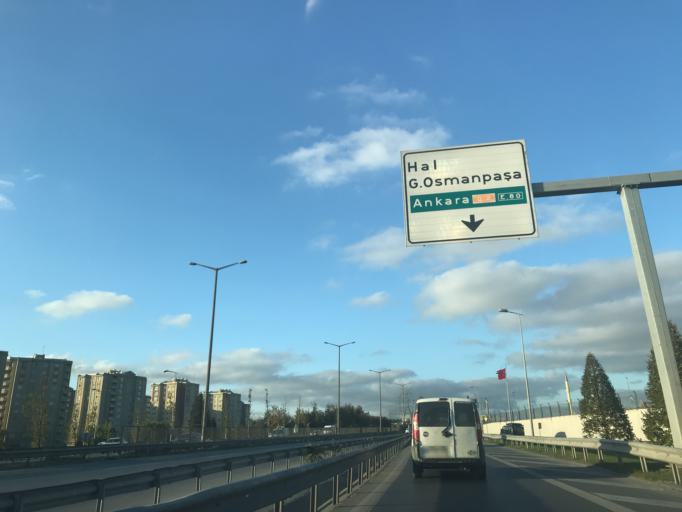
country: TR
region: Istanbul
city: Esenler
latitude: 41.0457
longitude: 28.8854
